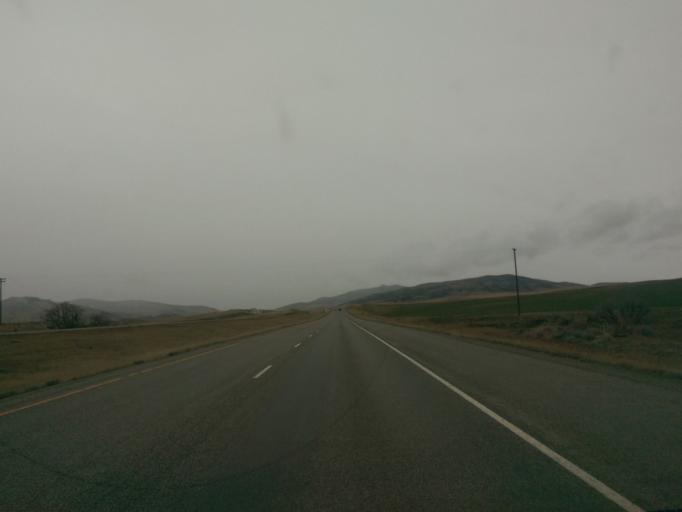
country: US
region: Montana
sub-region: Gallatin County
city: Three Forks
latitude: 45.9137
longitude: -111.7619
